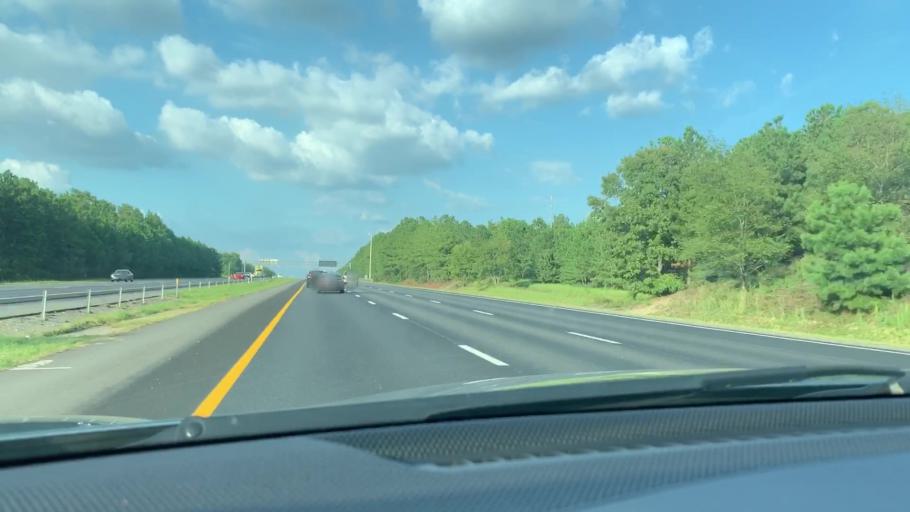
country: US
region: South Carolina
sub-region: Richland County
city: Woodfield
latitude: 34.0267
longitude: -80.9431
